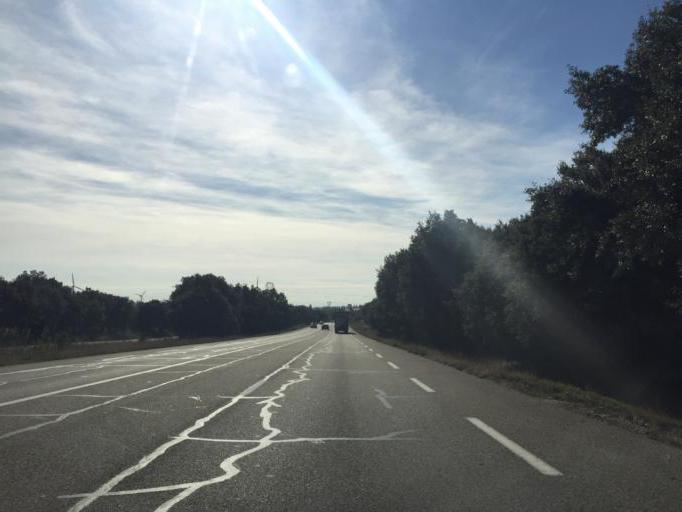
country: FR
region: Rhone-Alpes
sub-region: Departement de la Drome
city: Malataverne
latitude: 44.4577
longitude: 4.7540
